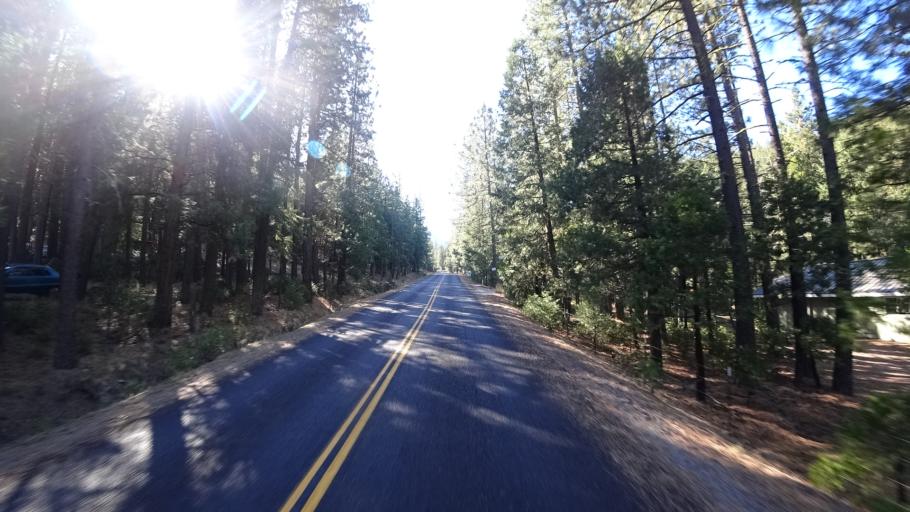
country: US
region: California
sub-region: Siskiyou County
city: Weed
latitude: 41.4233
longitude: -122.5008
